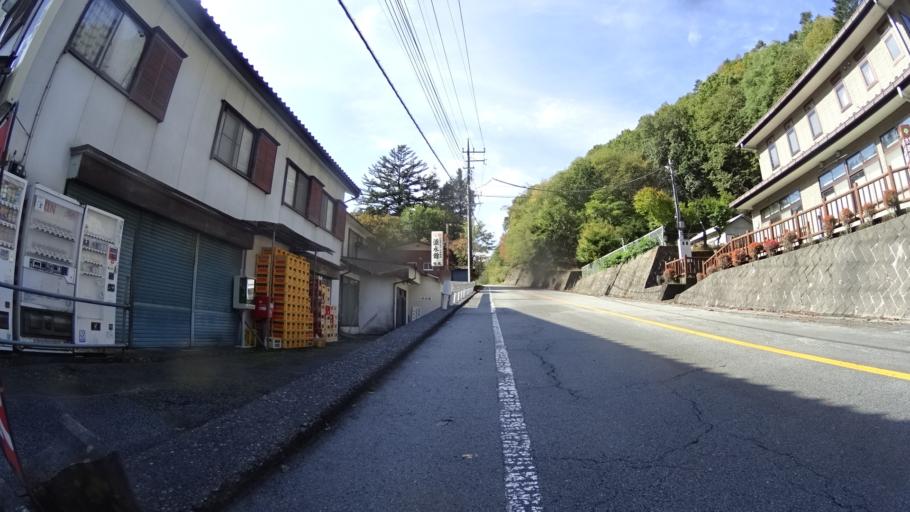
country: JP
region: Yamanashi
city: Enzan
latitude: 35.8050
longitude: 138.8265
